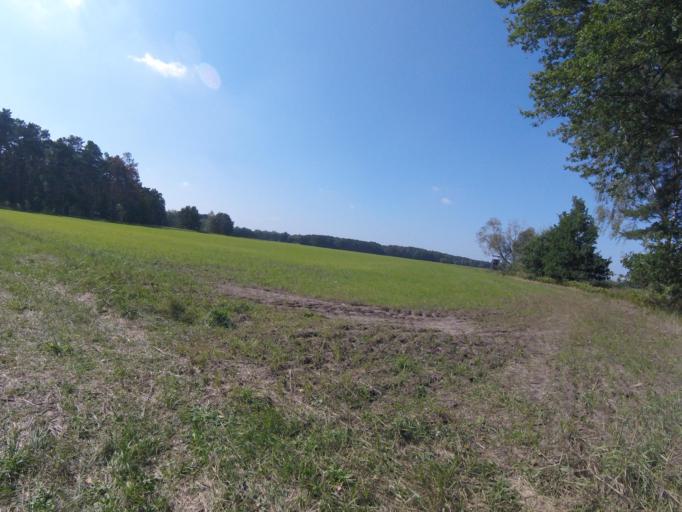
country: DE
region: Brandenburg
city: Mittenwalde
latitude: 52.2253
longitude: 13.5889
